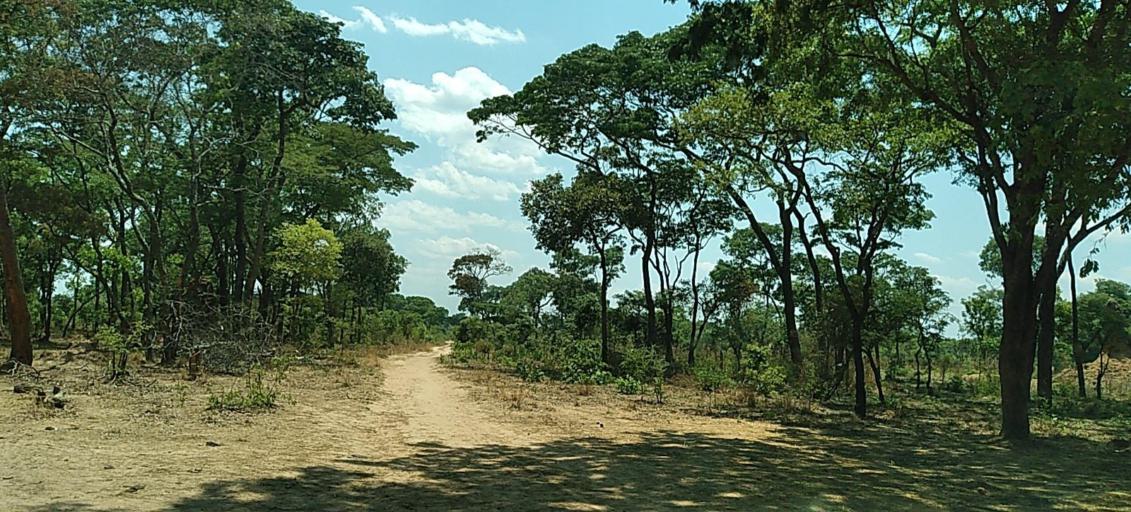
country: ZM
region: Central
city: Kapiri Mposhi
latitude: -13.6329
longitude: 28.7586
